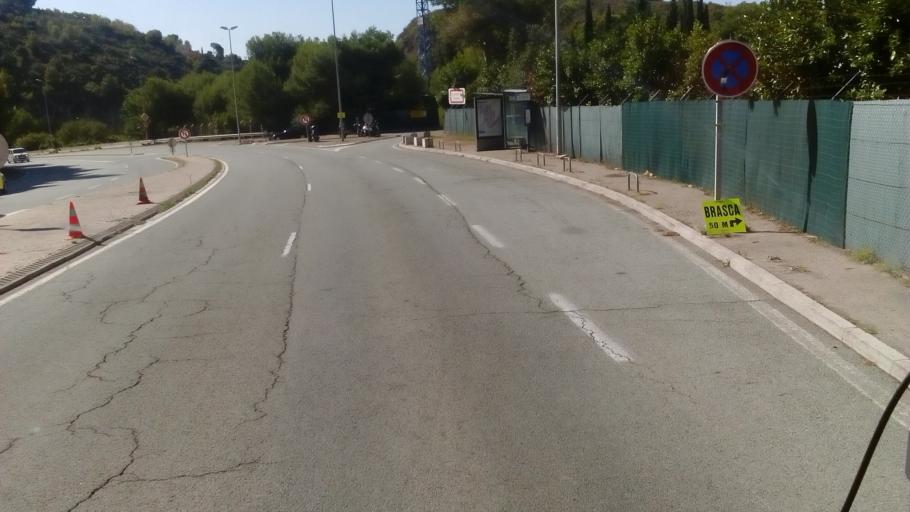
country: FR
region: Provence-Alpes-Cote d'Azur
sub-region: Departement des Alpes-Maritimes
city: La Turbie
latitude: 43.7317
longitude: 7.3904
